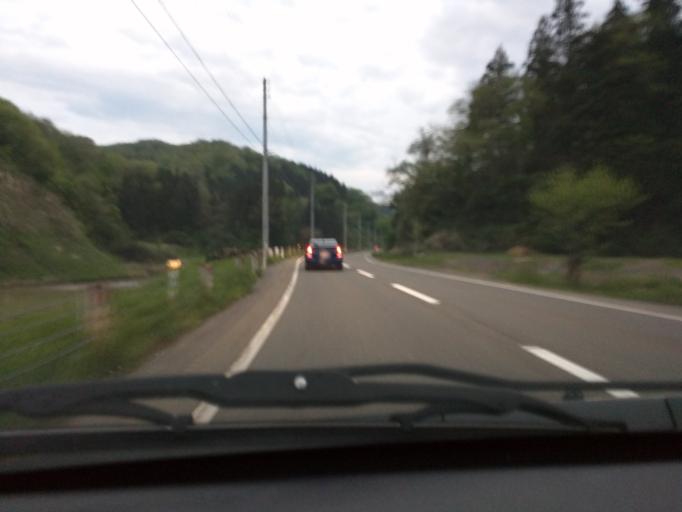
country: JP
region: Niigata
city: Ojiya
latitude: 37.3207
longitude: 138.6958
